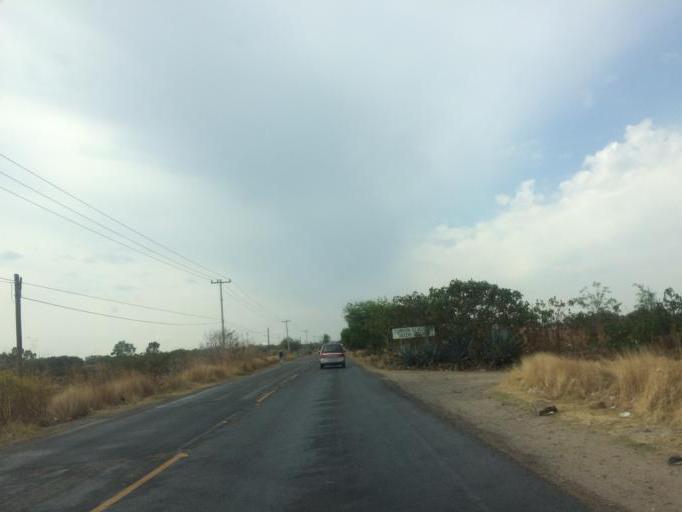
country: MX
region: Guanajuato
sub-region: Leon
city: Ladrilleras del Refugio
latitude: 21.0822
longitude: -101.5436
